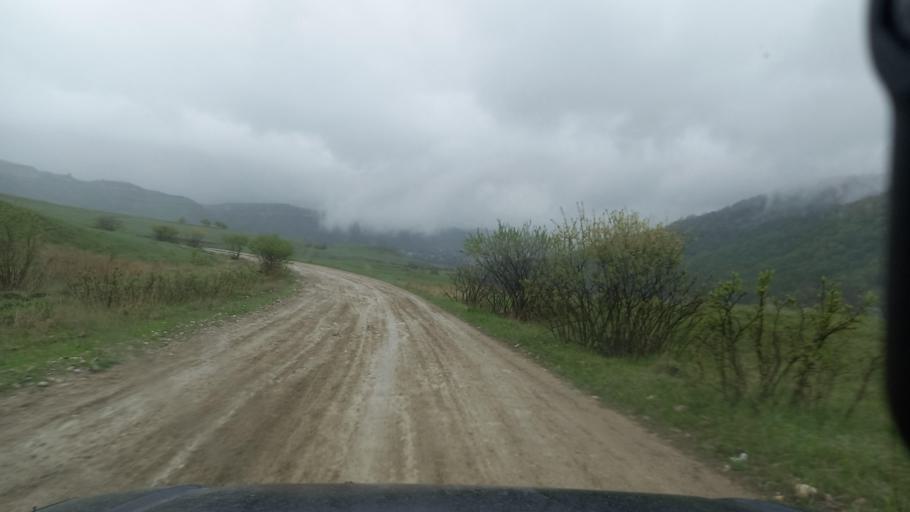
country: RU
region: Kabardino-Balkariya
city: Gundelen
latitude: 43.5939
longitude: 43.1276
